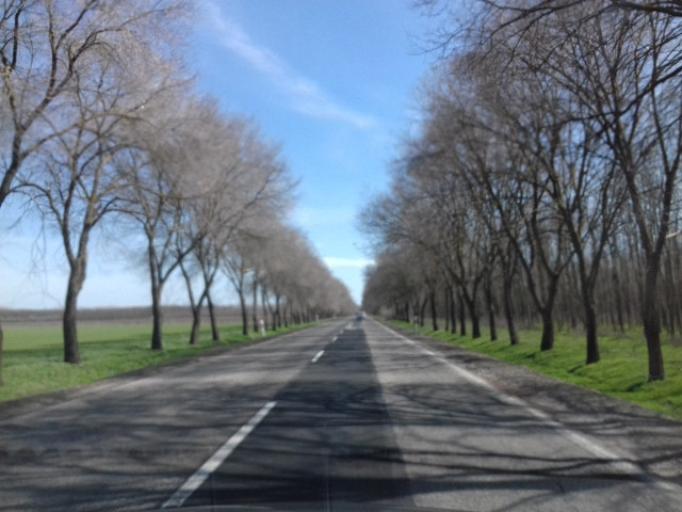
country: HU
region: Bacs-Kiskun
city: Nyarlorinc
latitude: 46.8984
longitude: 19.8222
